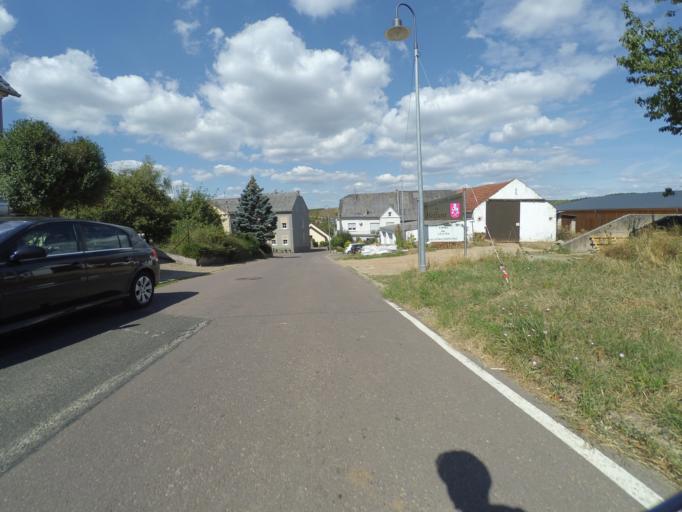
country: LU
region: Grevenmacher
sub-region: Canton de Grevenmacher
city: Wormeldange
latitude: 49.5859
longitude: 6.4152
